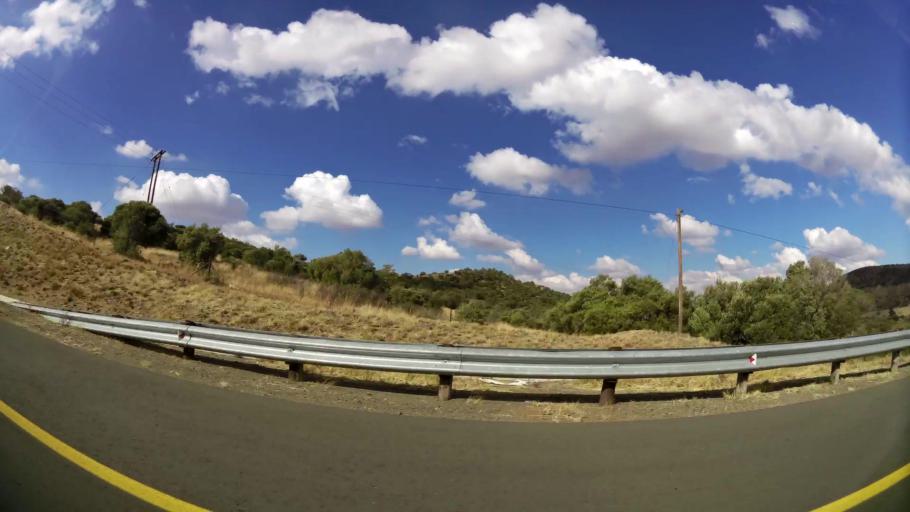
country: ZA
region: Orange Free State
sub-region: Mangaung Metropolitan Municipality
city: Bloemfontein
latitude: -29.1571
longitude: 26.0577
